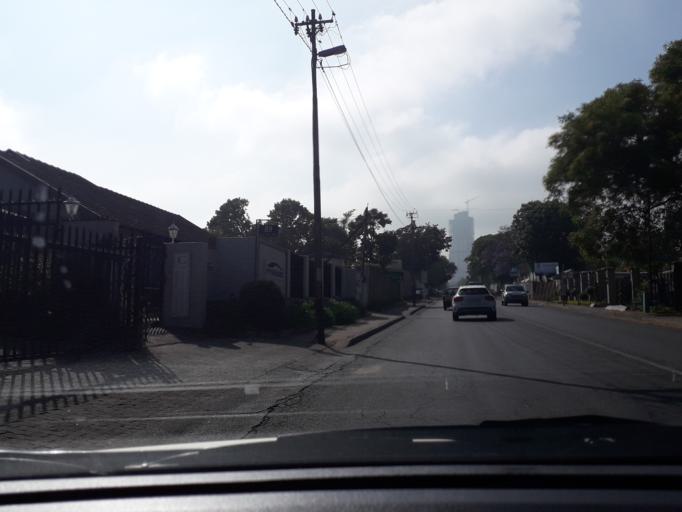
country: ZA
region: Gauteng
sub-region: City of Johannesburg Metropolitan Municipality
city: Johannesburg
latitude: -26.0959
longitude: 28.0407
